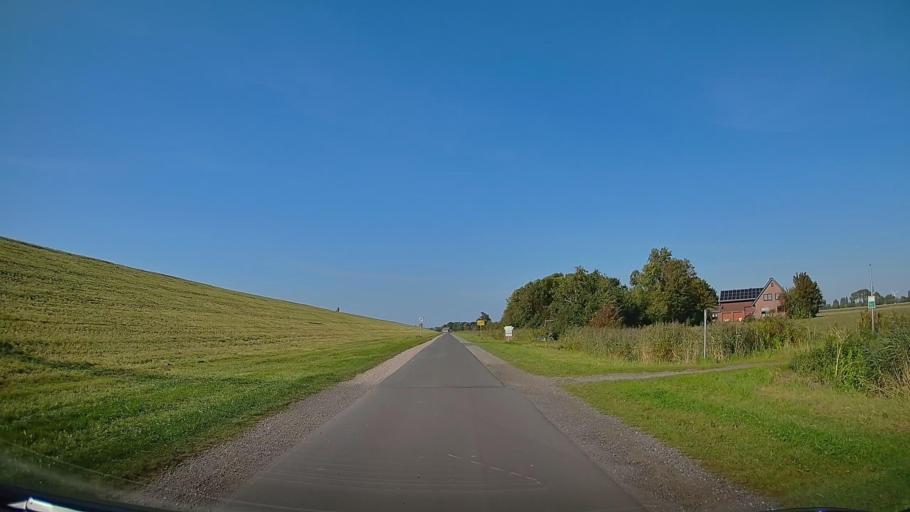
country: DE
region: Lower Saxony
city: Wremen
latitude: 53.6499
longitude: 8.4951
